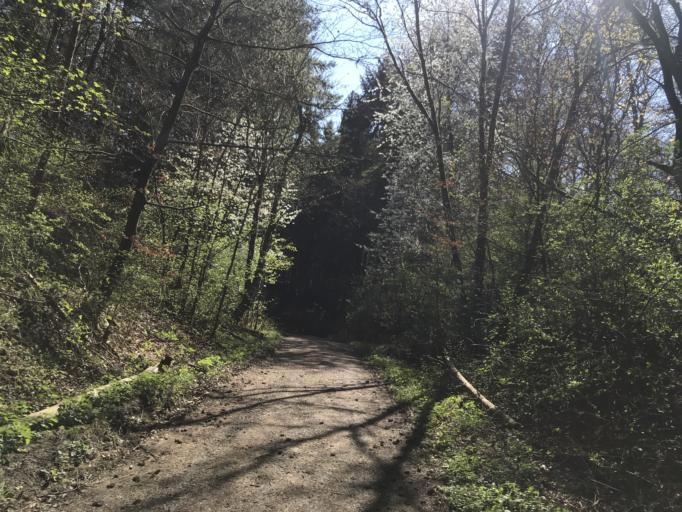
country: DE
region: Hesse
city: Beuern
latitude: 50.6566
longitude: 8.8043
